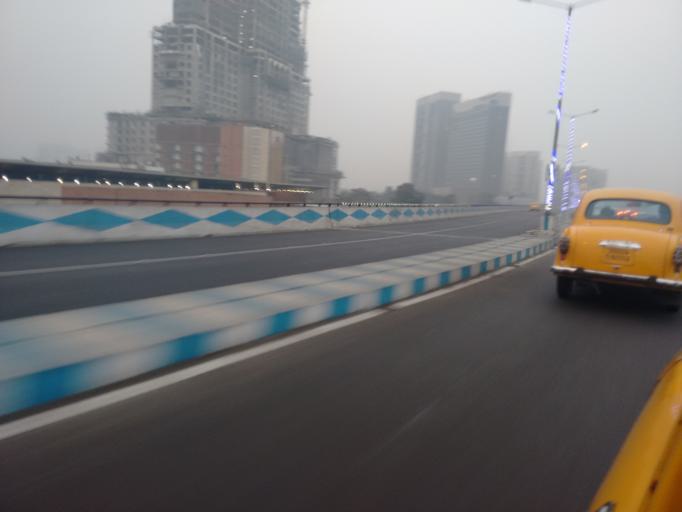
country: IN
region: West Bengal
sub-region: Kolkata
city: Kolkata
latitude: 22.5435
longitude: 88.3988
